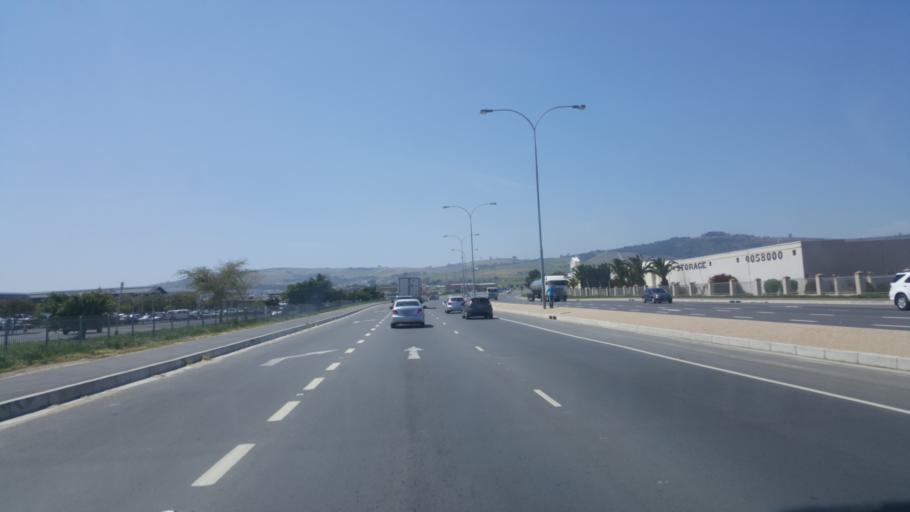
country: ZA
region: Western Cape
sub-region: City of Cape Town
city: Kraaifontein
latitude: -33.9511
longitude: 18.6964
